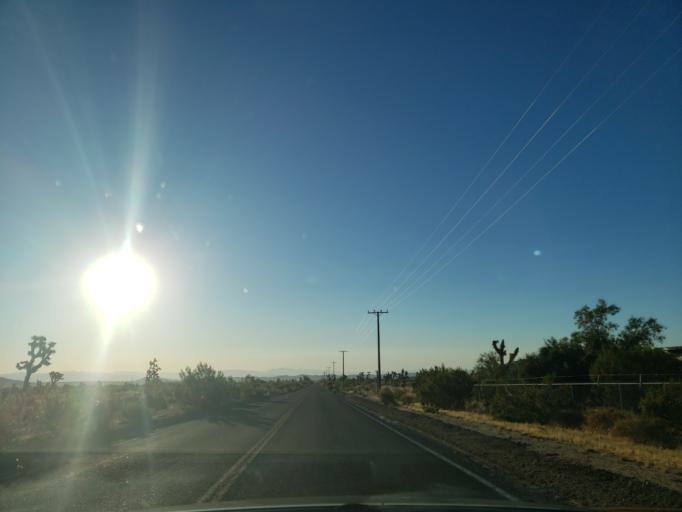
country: US
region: California
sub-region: San Bernardino County
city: Joshua Tree
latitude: 34.1930
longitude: -116.3825
